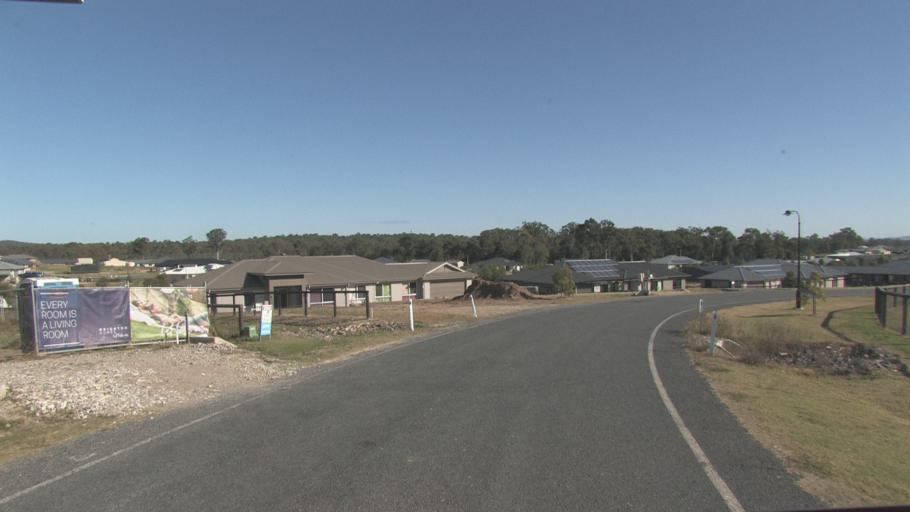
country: AU
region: Queensland
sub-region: Logan
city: Logan Reserve
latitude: -27.7489
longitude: 153.1406
